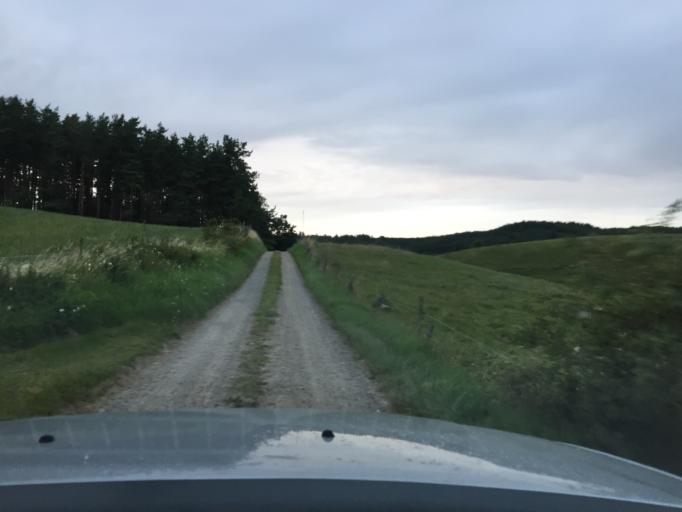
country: SE
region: Skane
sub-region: Kristianstads Kommun
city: Degeberga
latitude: 55.7226
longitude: 14.1273
